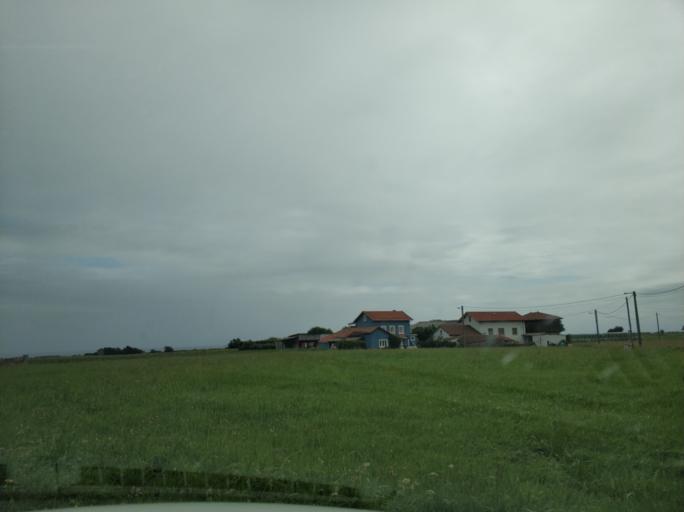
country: ES
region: Asturias
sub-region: Province of Asturias
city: Salas
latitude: 43.5527
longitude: -6.3787
